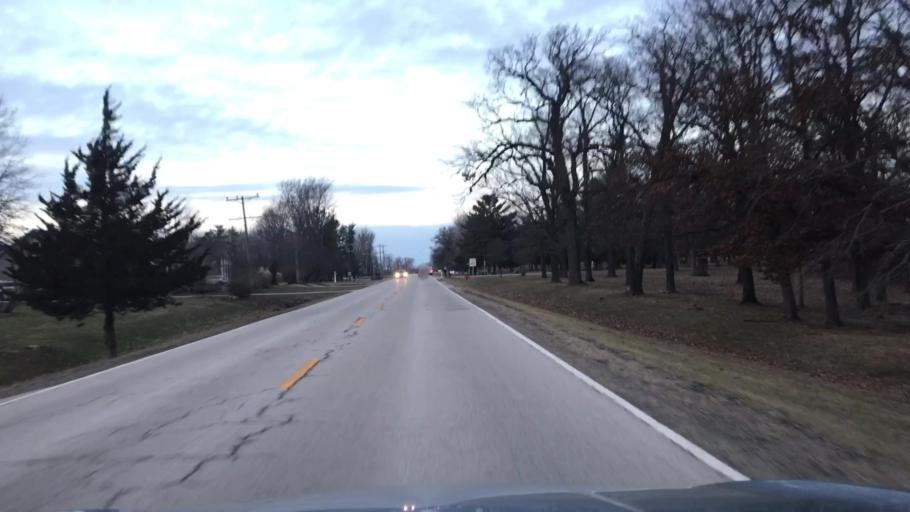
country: US
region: Illinois
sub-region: McLean County
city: Hudson
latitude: 40.6533
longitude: -88.9369
